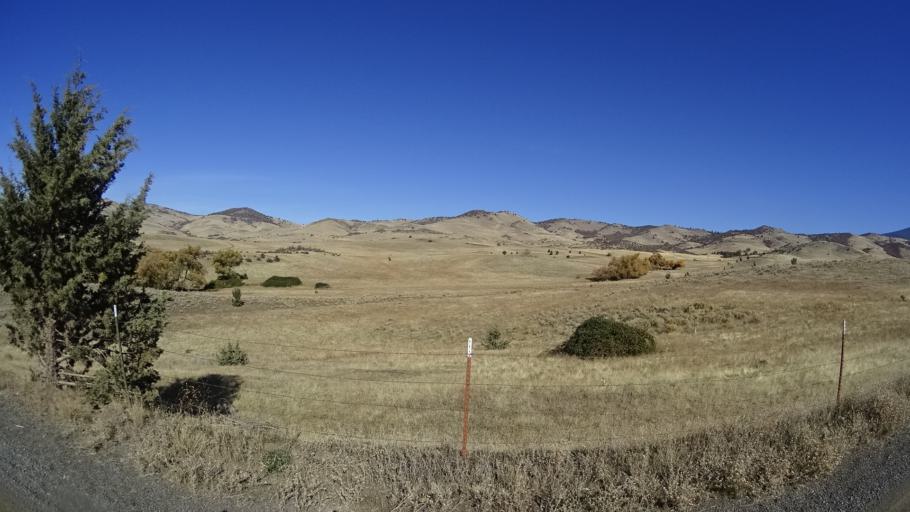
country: US
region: California
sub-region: Siskiyou County
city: Montague
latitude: 41.8158
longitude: -122.3697
